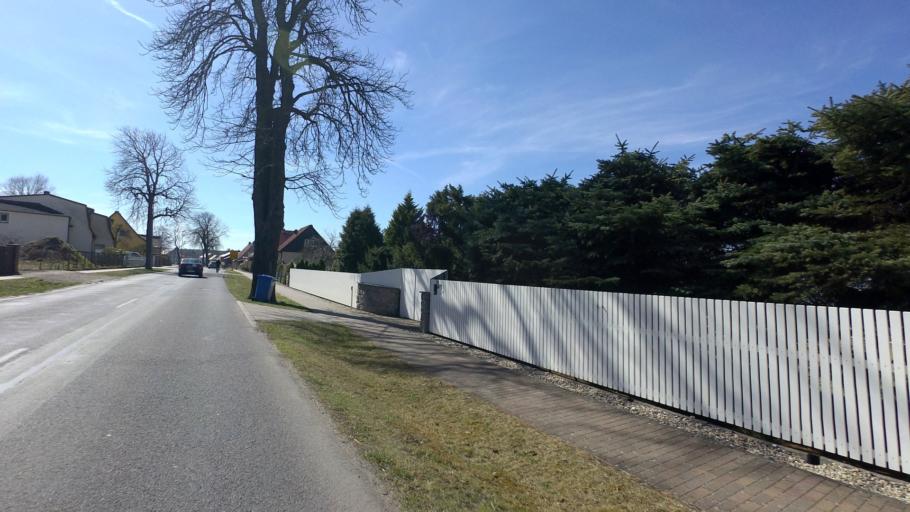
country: DE
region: Brandenburg
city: Mittenwalde
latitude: 52.2081
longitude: 13.5835
